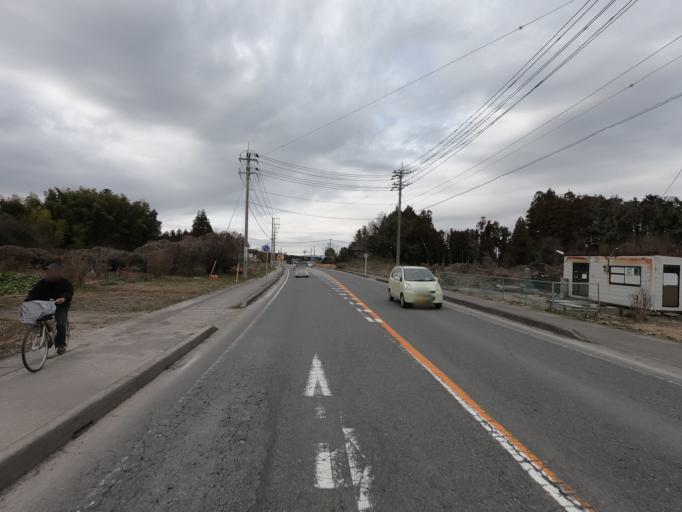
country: JP
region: Ibaraki
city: Ishioka
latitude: 36.0947
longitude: 140.3011
